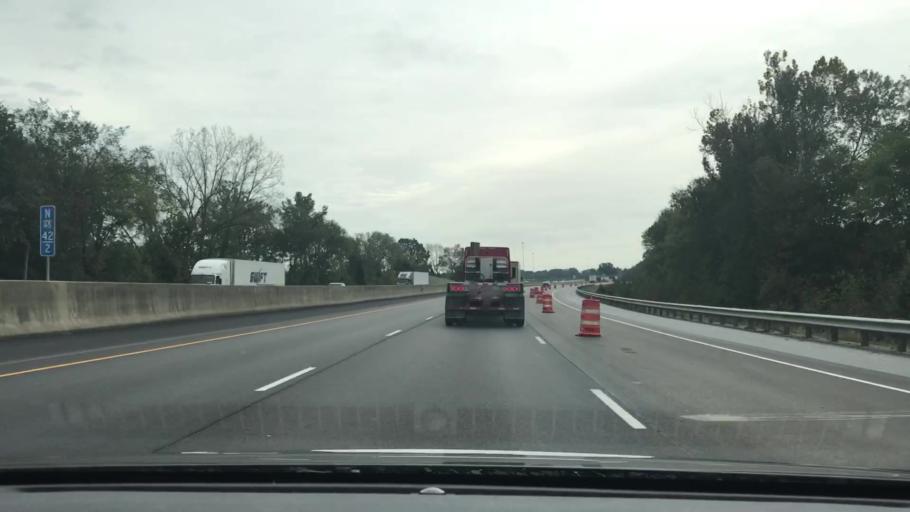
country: US
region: Kentucky
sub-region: Barren County
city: Cave City
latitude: 37.0557
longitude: -86.1274
